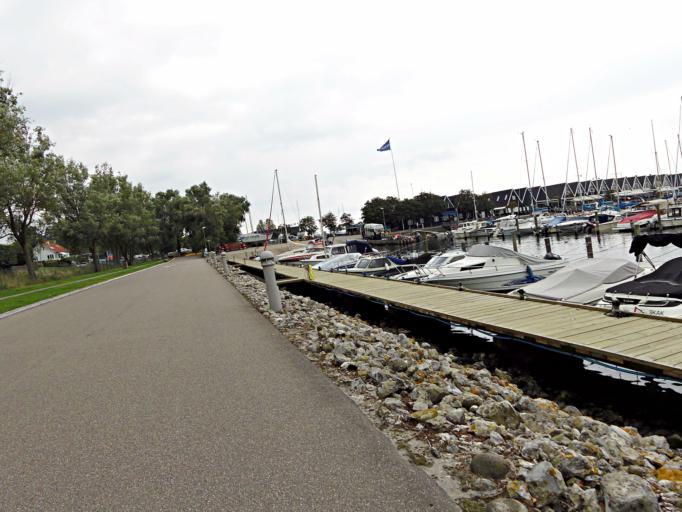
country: DK
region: Capital Region
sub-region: Horsholm Kommune
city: Horsholm
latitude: 55.8836
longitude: 12.5446
